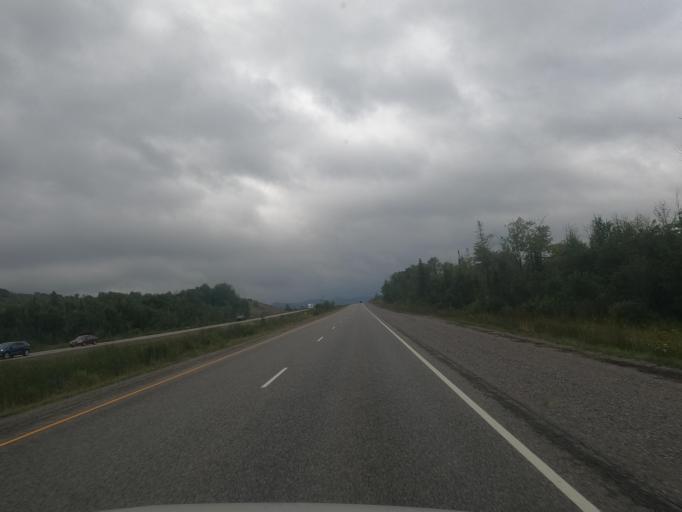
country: CA
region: Ontario
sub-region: Algoma
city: Sault Ste. Marie
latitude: 46.5217
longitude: -84.0737
